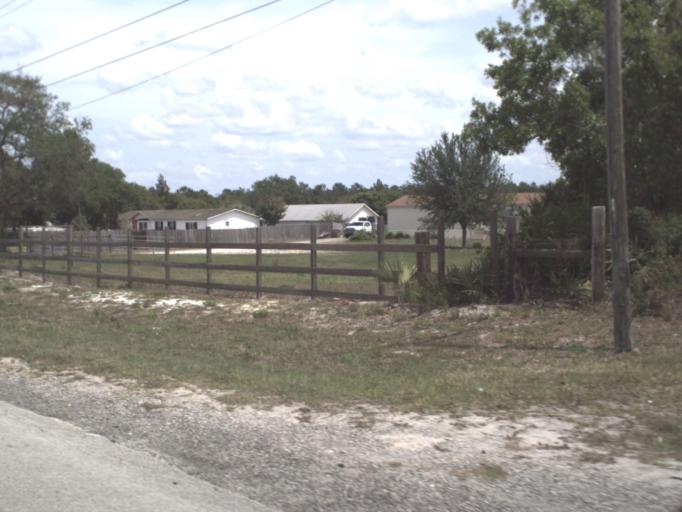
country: US
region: Florida
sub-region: Lake County
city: Lake Mack-Forest Hills
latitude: 28.9654
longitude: -81.4115
